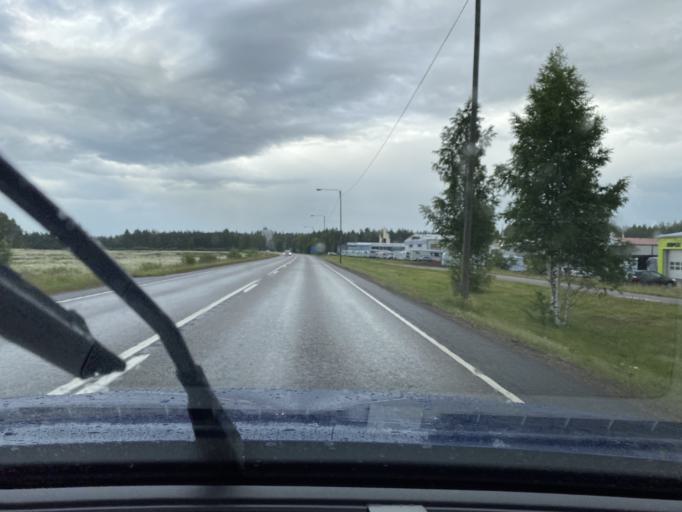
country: FI
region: Uusimaa
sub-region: Helsinki
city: Hyvinge
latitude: 60.6123
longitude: 24.8091
